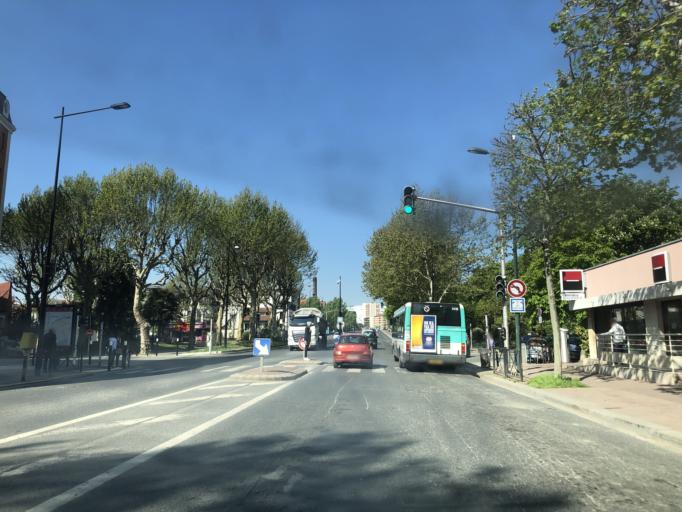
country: FR
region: Ile-de-France
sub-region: Departement du Val-de-Marne
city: Joinville-le-Pont
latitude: 48.8201
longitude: 2.4751
